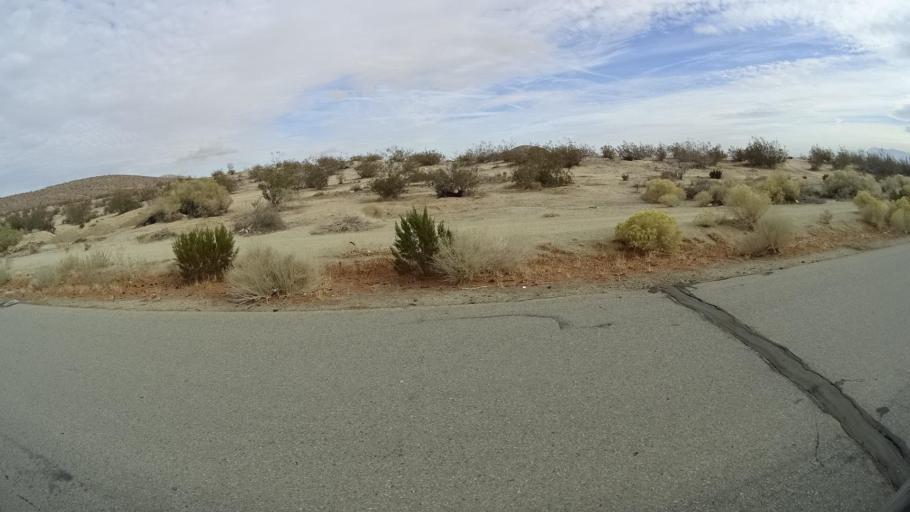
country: US
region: California
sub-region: Kern County
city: Rosamond
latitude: 34.8743
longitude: -118.1495
